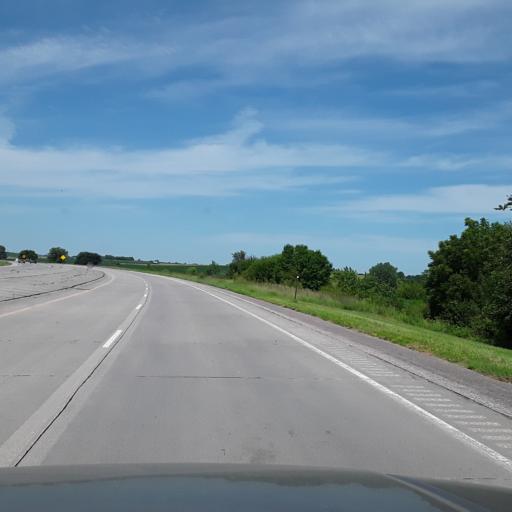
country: US
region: Nebraska
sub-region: Lancaster County
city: Lincoln
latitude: 40.8881
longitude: -96.7984
